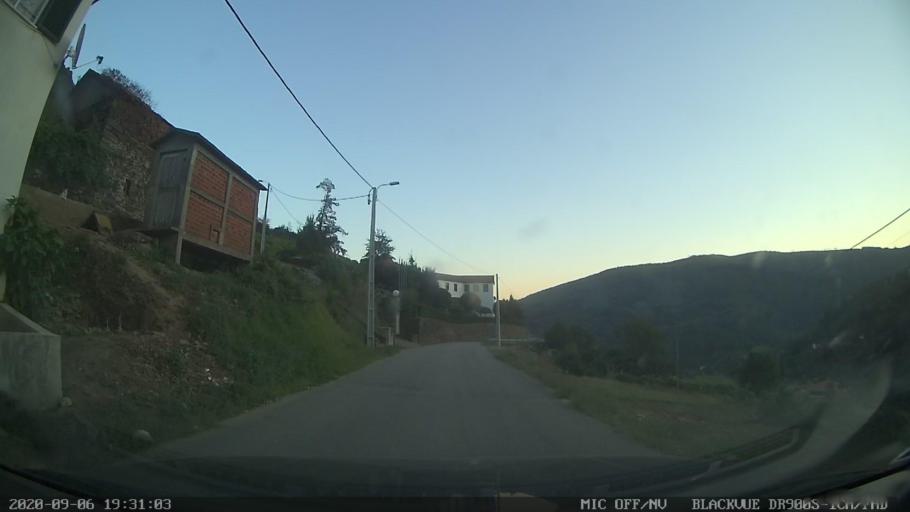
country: PT
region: Vila Real
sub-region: Mesao Frio
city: Mesao Frio
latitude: 41.1832
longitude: -7.9011
